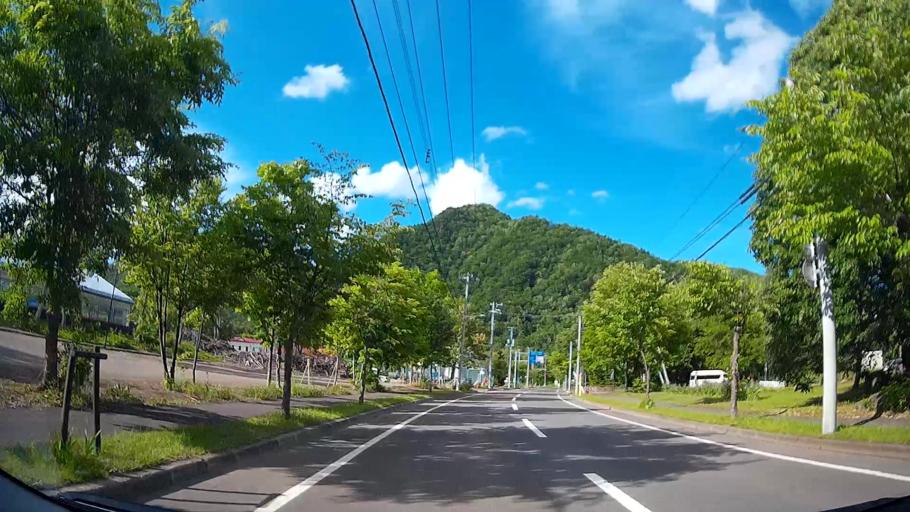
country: JP
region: Hokkaido
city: Sapporo
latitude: 42.9712
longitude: 141.1647
